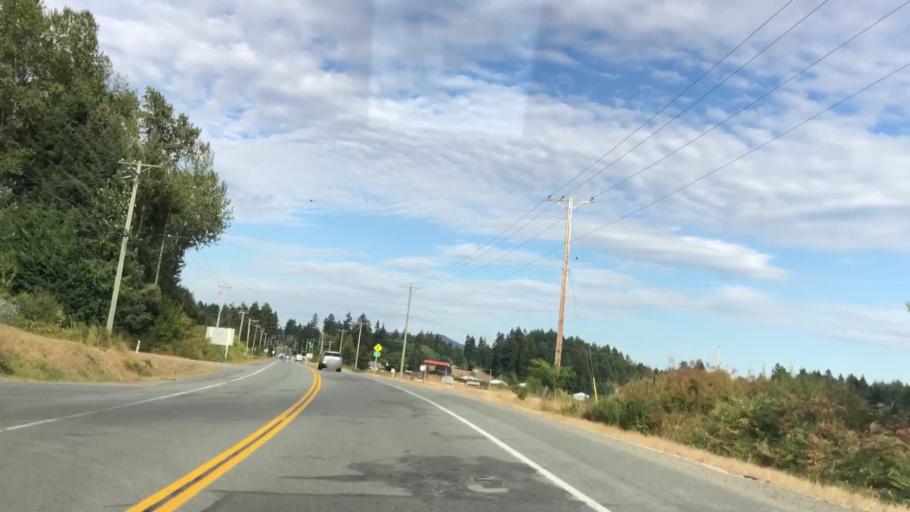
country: CA
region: British Columbia
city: Duncan
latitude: 48.8143
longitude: -123.7266
